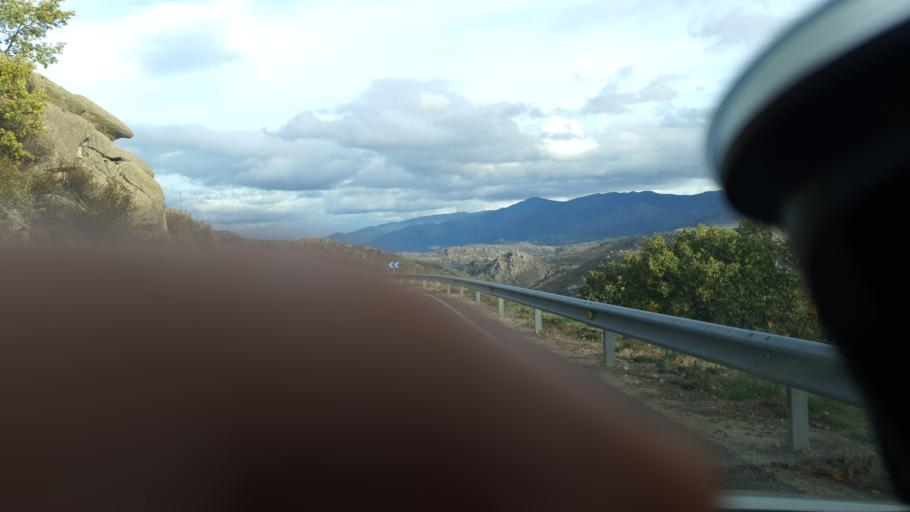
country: ES
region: Castille and Leon
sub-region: Provincia de Avila
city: Navalosa
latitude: 40.3940
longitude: -4.9093
